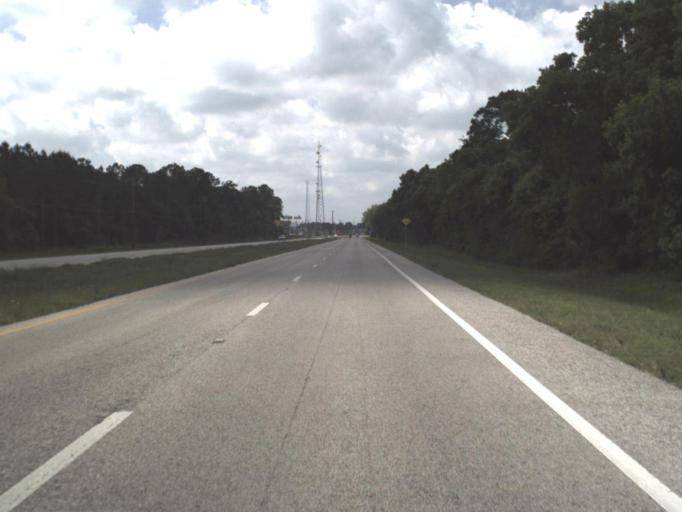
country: US
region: Florida
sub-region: Flagler County
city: Palm Coast
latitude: 29.6712
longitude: -81.2902
